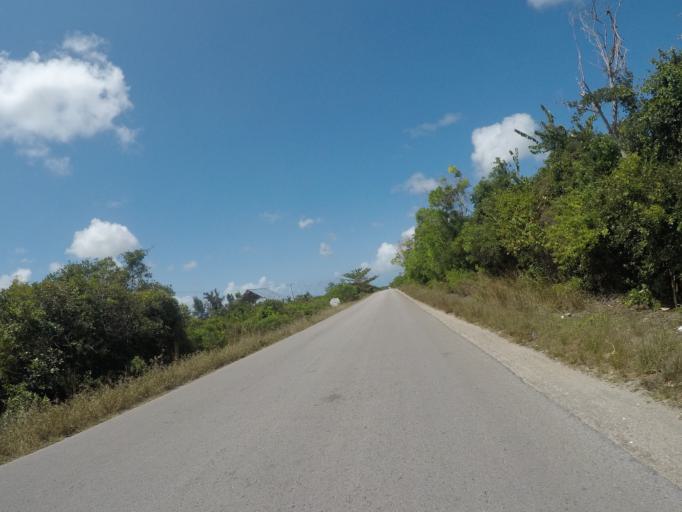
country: TZ
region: Zanzibar Central/South
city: Nganane
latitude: -6.2791
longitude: 39.4787
